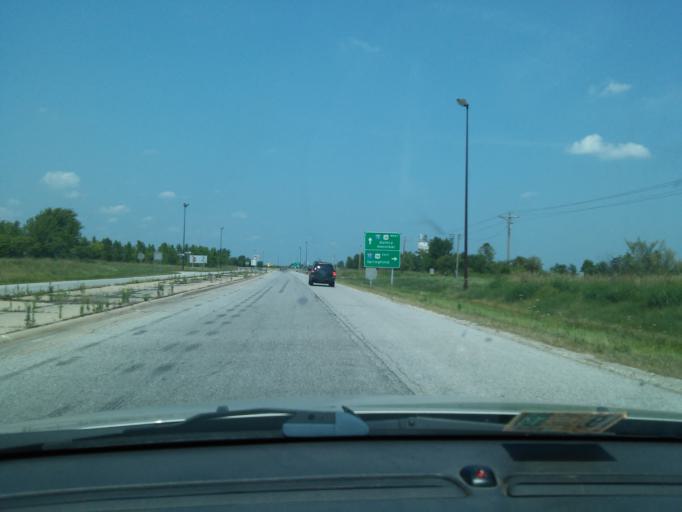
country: US
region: Illinois
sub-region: Pike County
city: Griggsville
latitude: 39.6716
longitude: -90.7689
